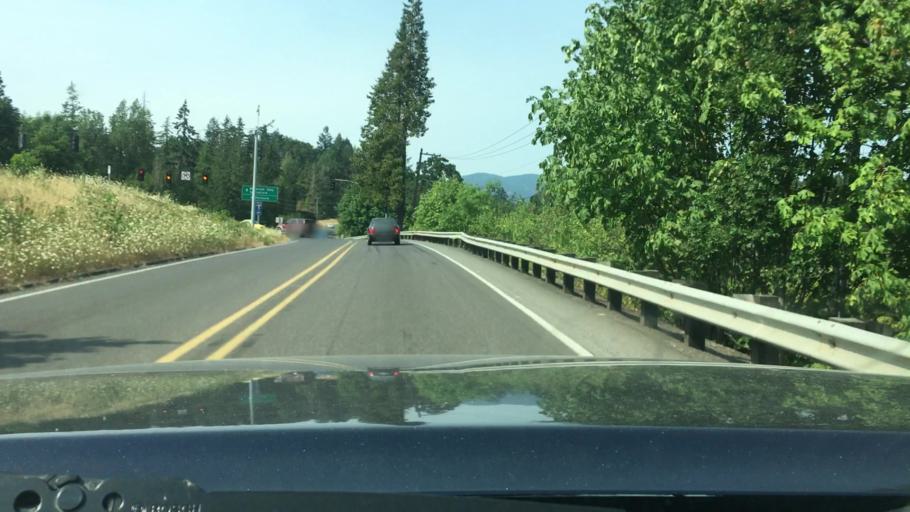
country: US
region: Oregon
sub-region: Lane County
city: Springfield
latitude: 44.0235
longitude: -123.0267
